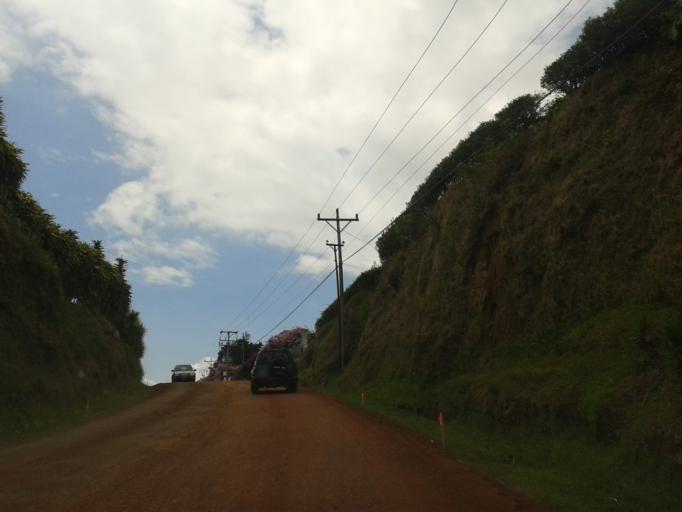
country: CR
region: Alajuela
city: Sabanilla
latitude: 10.0929
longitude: -84.1885
